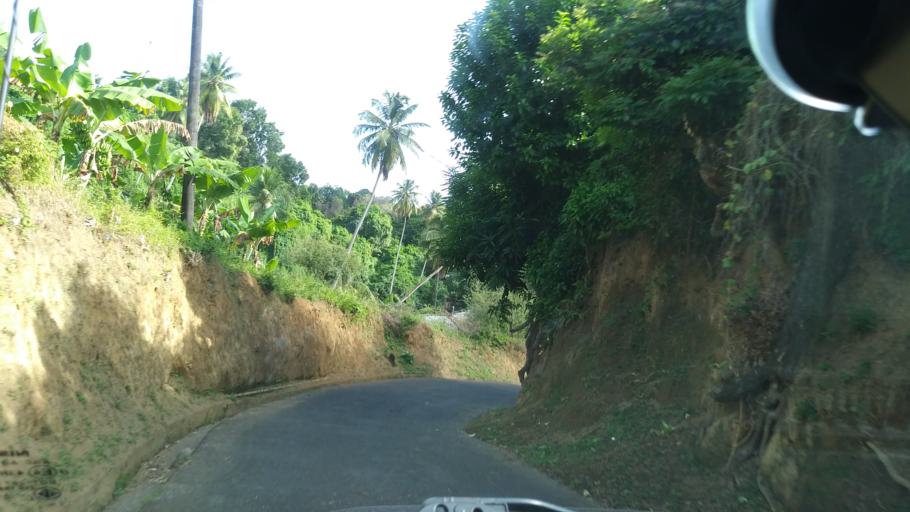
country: VC
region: Charlotte
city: Byera Village
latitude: 13.2392
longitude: -61.1334
